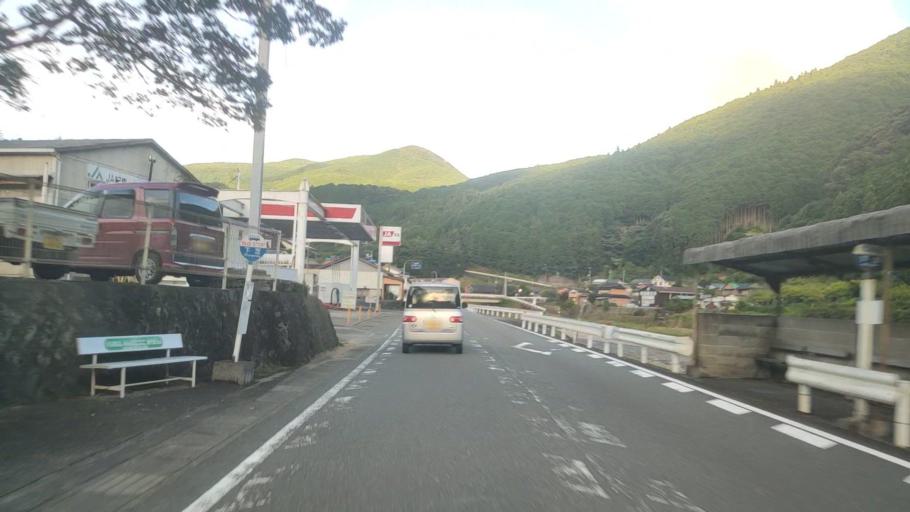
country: JP
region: Wakayama
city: Tanabe
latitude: 33.7874
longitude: 135.5102
